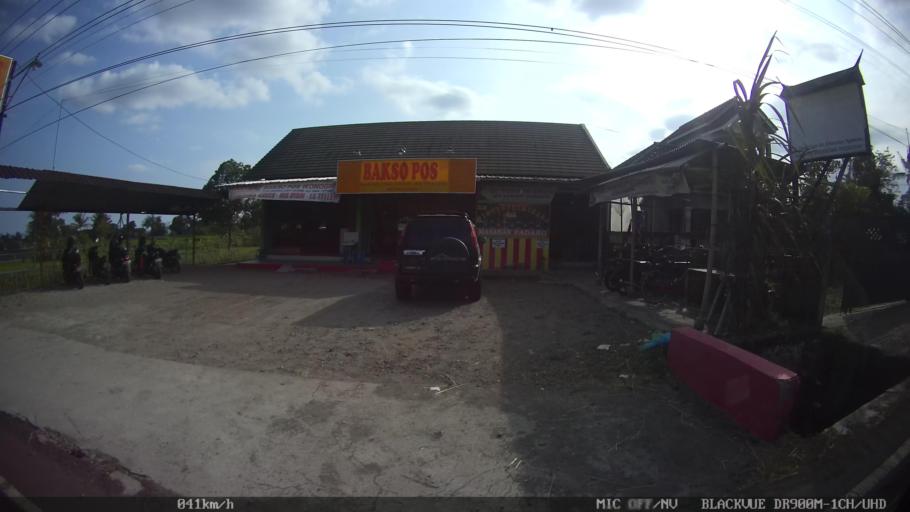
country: ID
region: Central Java
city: Candi Prambanan
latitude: -7.6959
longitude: 110.4639
